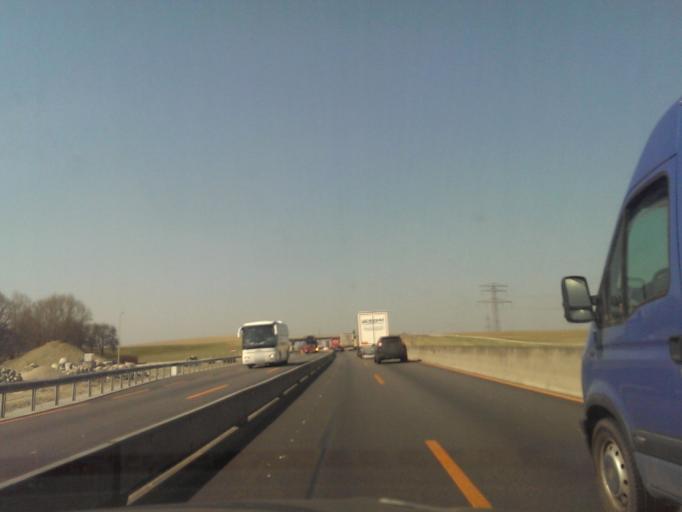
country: AT
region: Upper Austria
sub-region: Politischer Bezirk Vocklabruck
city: Wolfsegg am Hausruck
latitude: 48.1839
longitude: 13.6895
